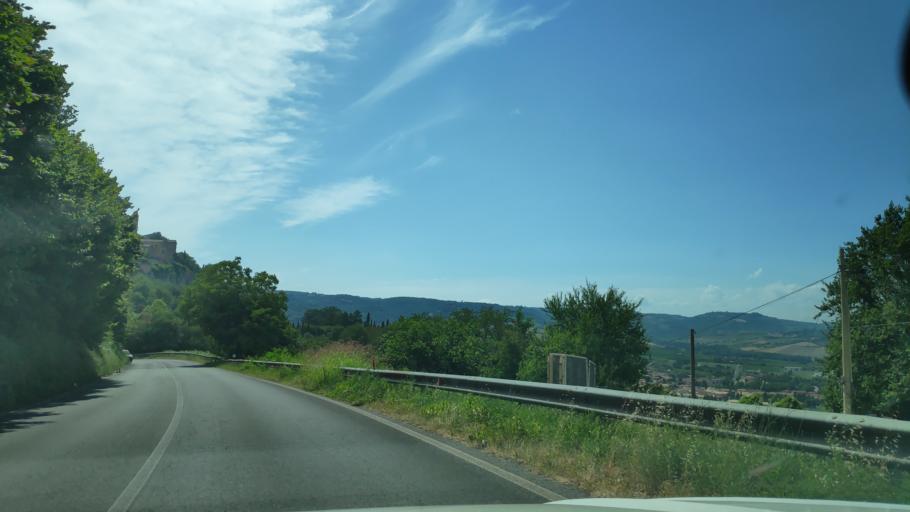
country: IT
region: Umbria
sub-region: Provincia di Terni
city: Orvieto
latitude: 42.7222
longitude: 12.1105
